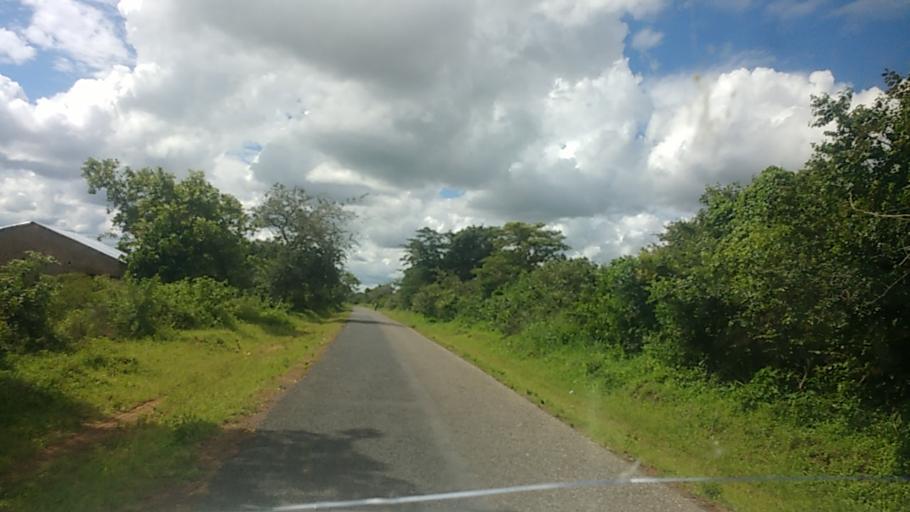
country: UG
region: Eastern Region
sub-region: Katakwi District
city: Katakwi
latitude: 1.8942
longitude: 33.9597
